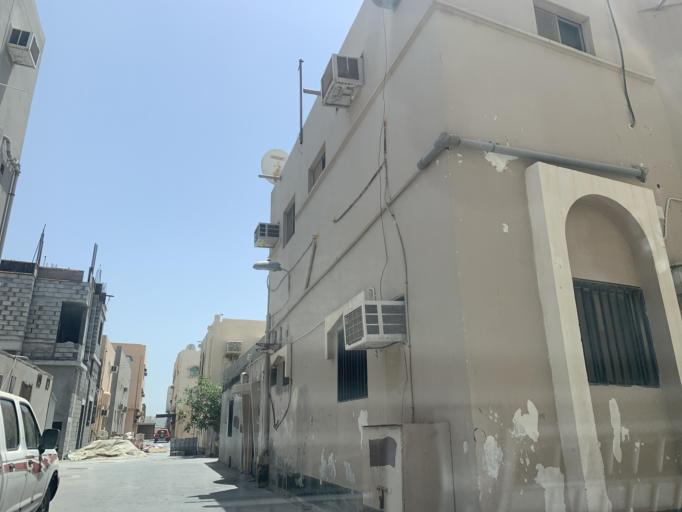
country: BH
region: Northern
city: Sitrah
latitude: 26.1587
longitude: 50.6217
